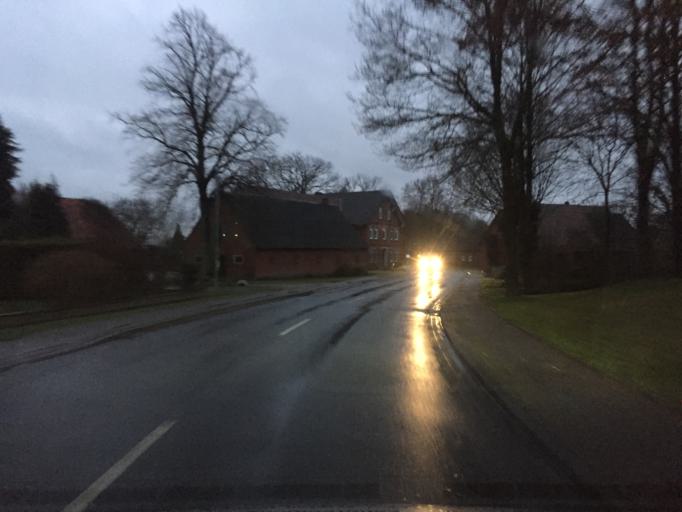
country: DE
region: Lower Saxony
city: Sudwalde
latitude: 52.7960
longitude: 8.8401
